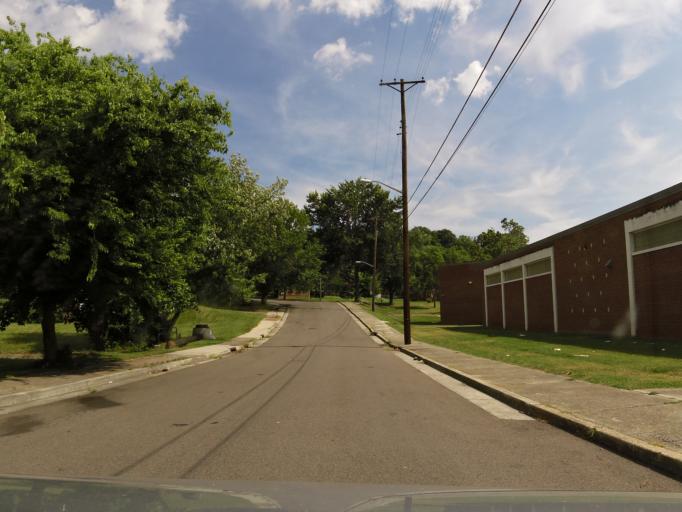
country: US
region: Tennessee
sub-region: Knox County
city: Knoxville
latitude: 35.9754
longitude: -83.9042
